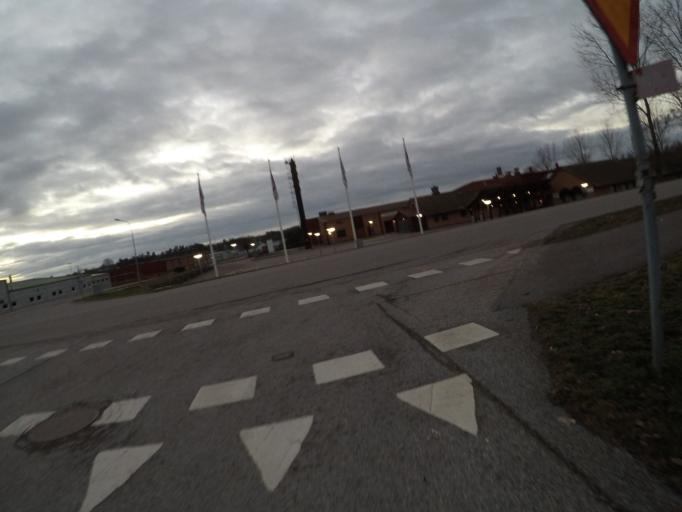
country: SE
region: Skane
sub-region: Sjobo Kommun
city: Sjoebo
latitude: 55.6417
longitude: 13.6919
